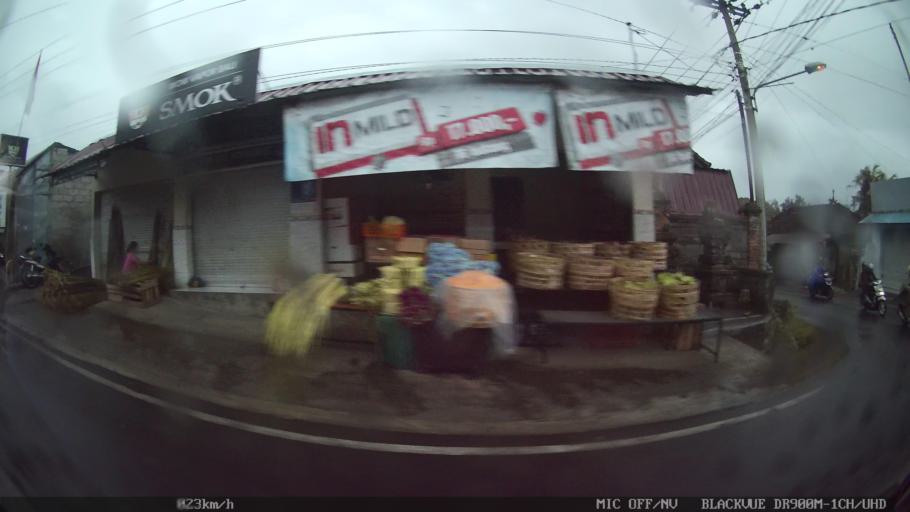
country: ID
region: Bali
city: Banjar Desa
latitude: -8.5759
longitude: 115.2588
